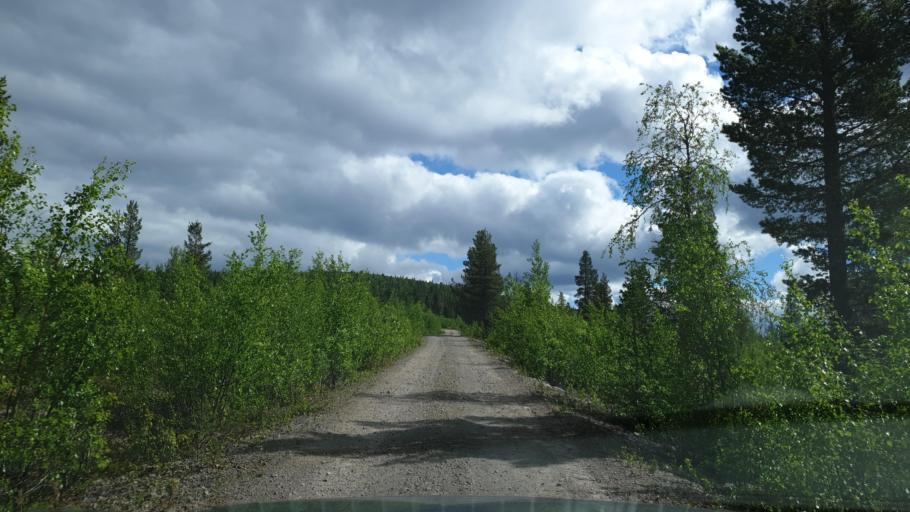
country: SE
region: Norrbotten
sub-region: Jokkmokks Kommun
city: Jokkmokk
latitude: 67.0312
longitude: 19.9992
